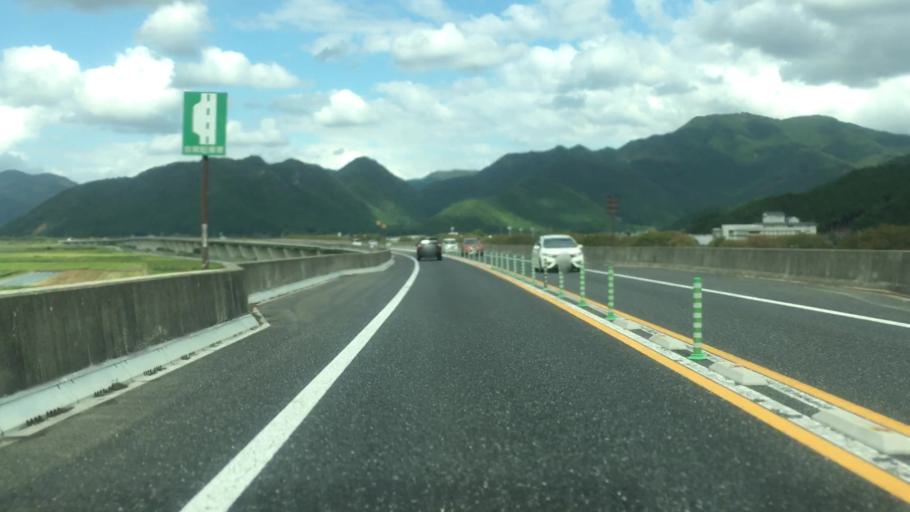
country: JP
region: Kyoto
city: Fukuchiyama
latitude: 35.1926
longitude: 135.0421
